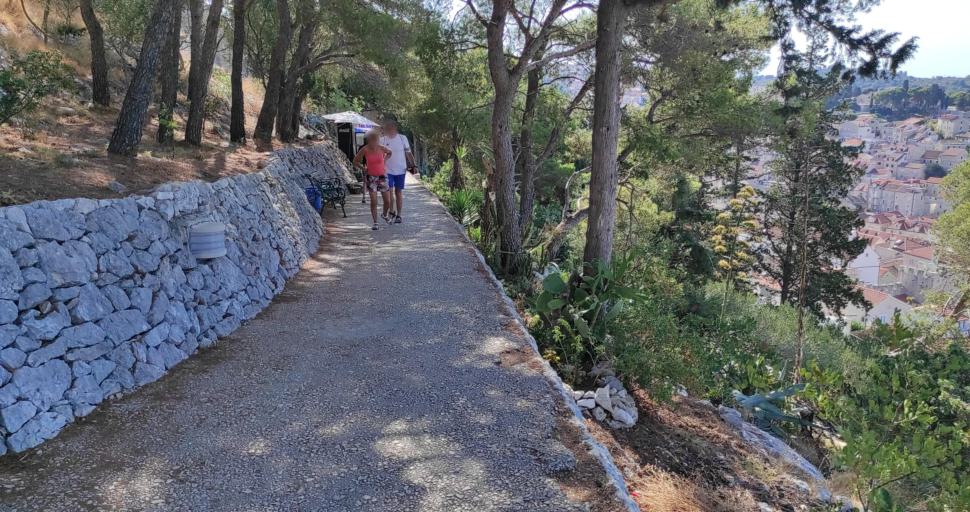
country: HR
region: Splitsko-Dalmatinska
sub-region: Grad Hvar
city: Hvar
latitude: 43.1745
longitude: 16.4409
